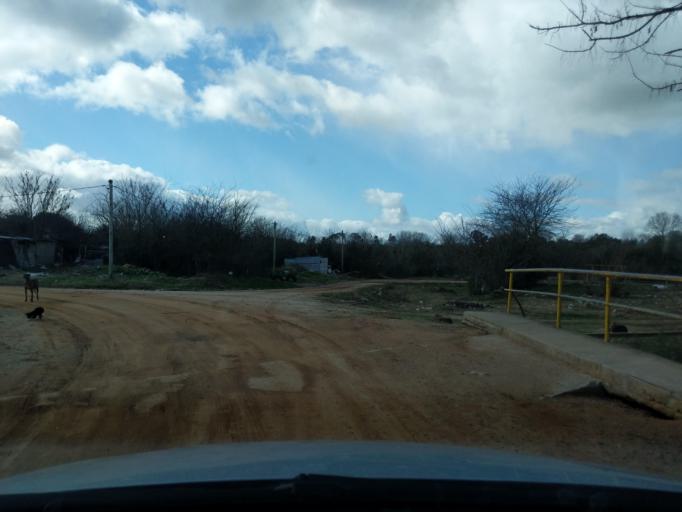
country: UY
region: Florida
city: Florida
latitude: -34.0959
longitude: -56.2064
